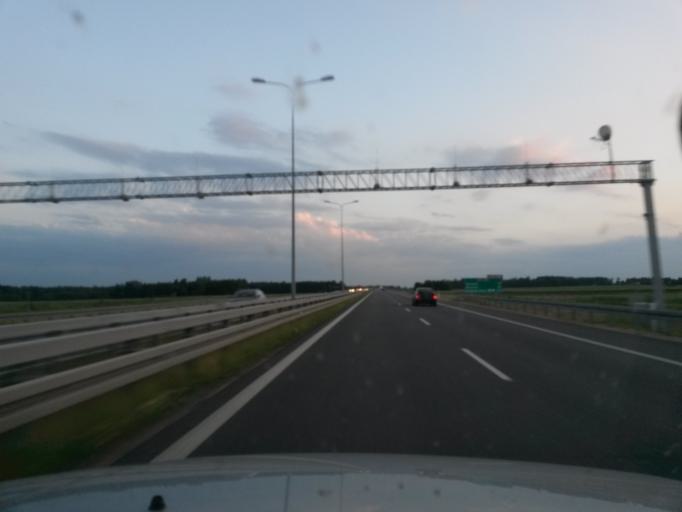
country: PL
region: Lower Silesian Voivodeship
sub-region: Powiat olesnicki
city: Twardogora
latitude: 51.2818
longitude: 17.5692
